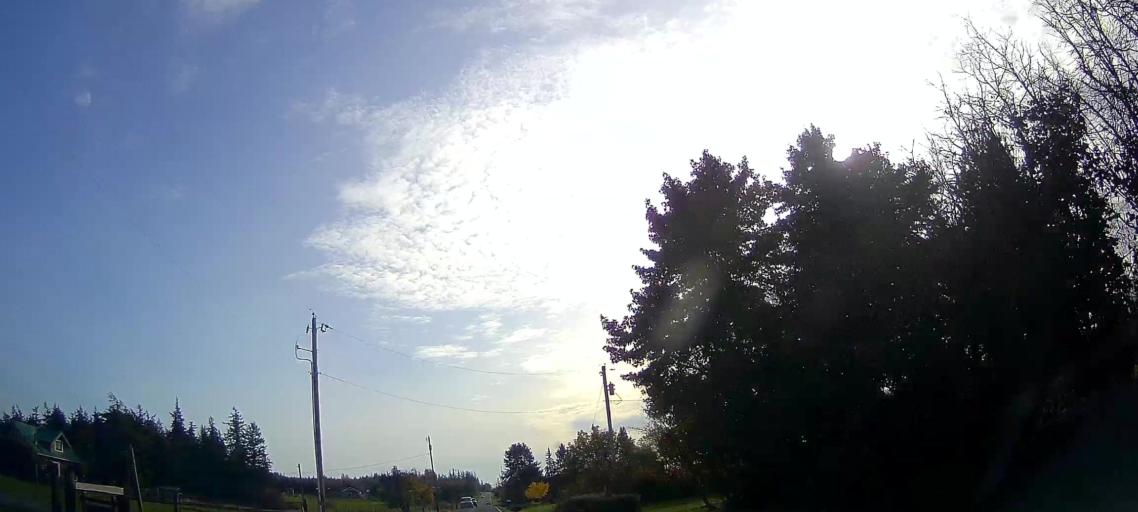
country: US
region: Washington
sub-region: Snohomish County
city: Stanwood
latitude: 48.2454
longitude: -122.4171
